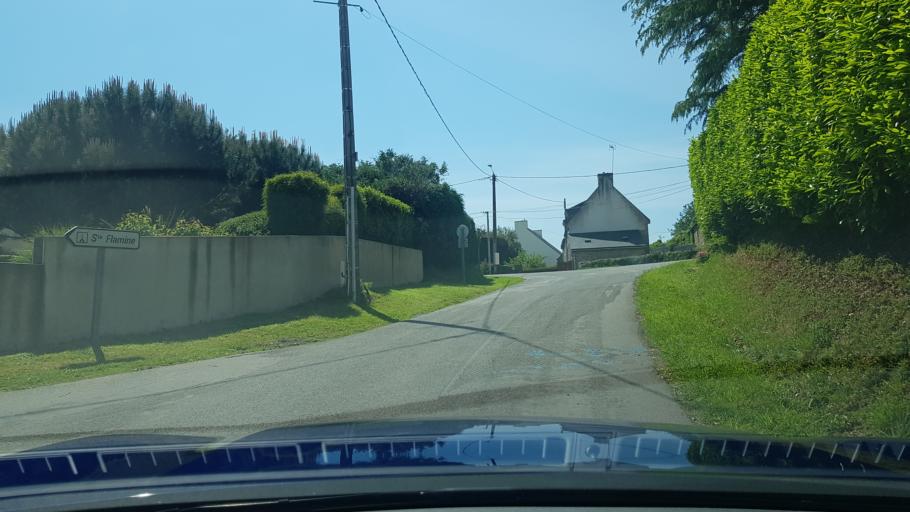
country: FR
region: Brittany
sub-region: Departement du Morbihan
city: Gestel
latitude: 47.8132
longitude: -3.4232
